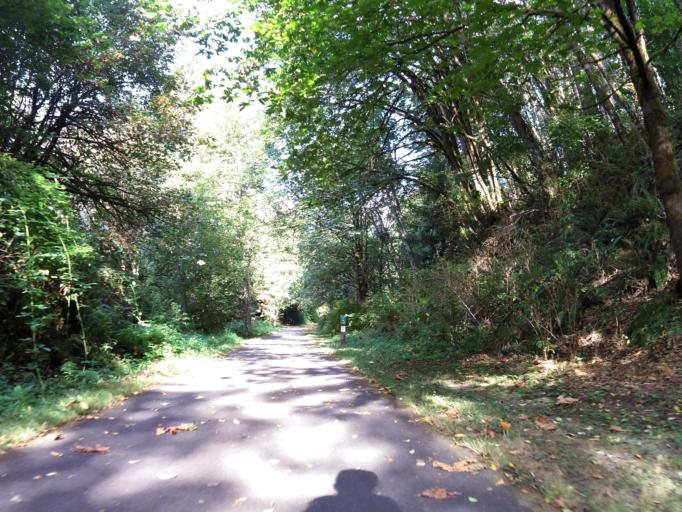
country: US
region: Washington
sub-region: Thurston County
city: Olympia
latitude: 47.0351
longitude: -122.8770
